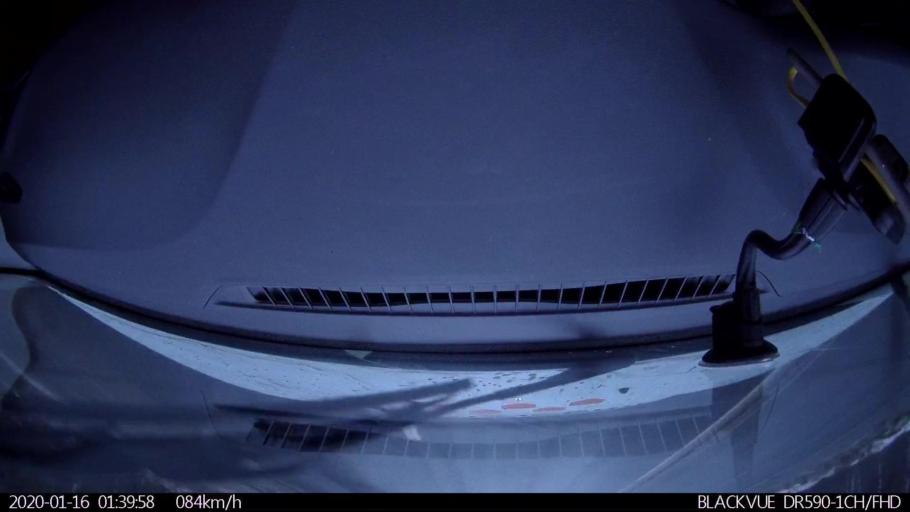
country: RU
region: Nizjnij Novgorod
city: Gorbatovka
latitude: 56.3305
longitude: 43.7868
